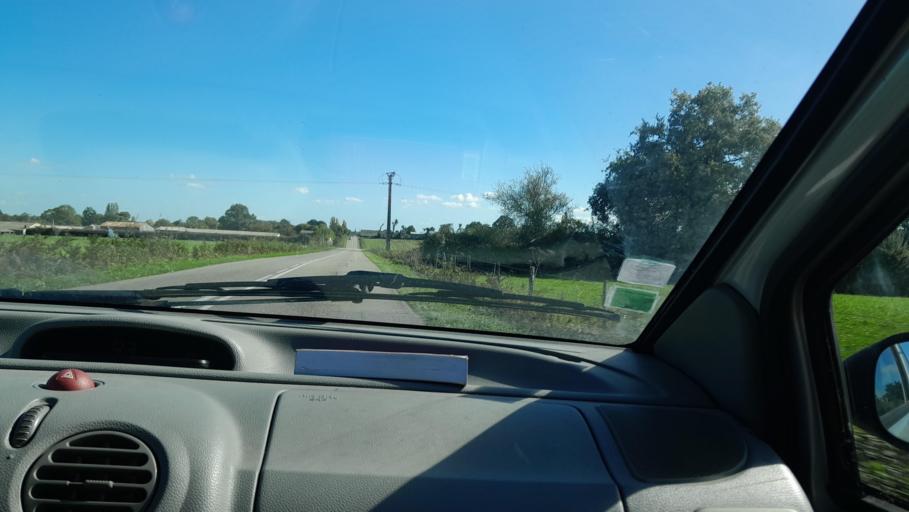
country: FR
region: Pays de la Loire
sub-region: Departement de la Mayenne
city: Quelaines-Saint-Gault
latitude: 47.9308
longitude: -0.8324
